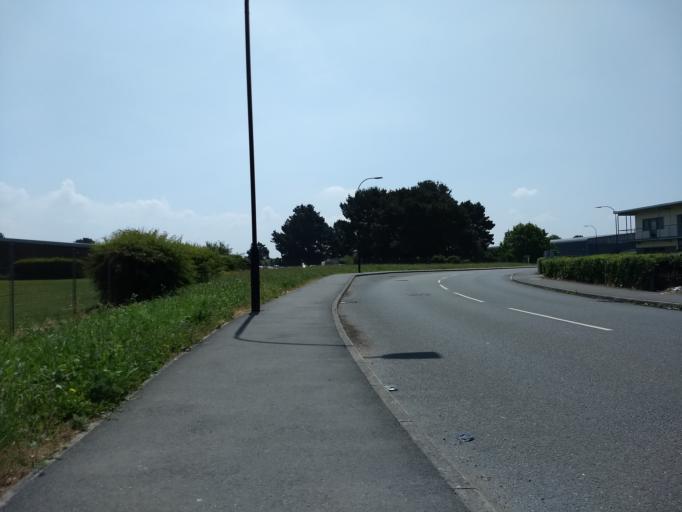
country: GB
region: England
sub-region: Isle of Wight
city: Northwood
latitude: 50.7516
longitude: -1.3072
